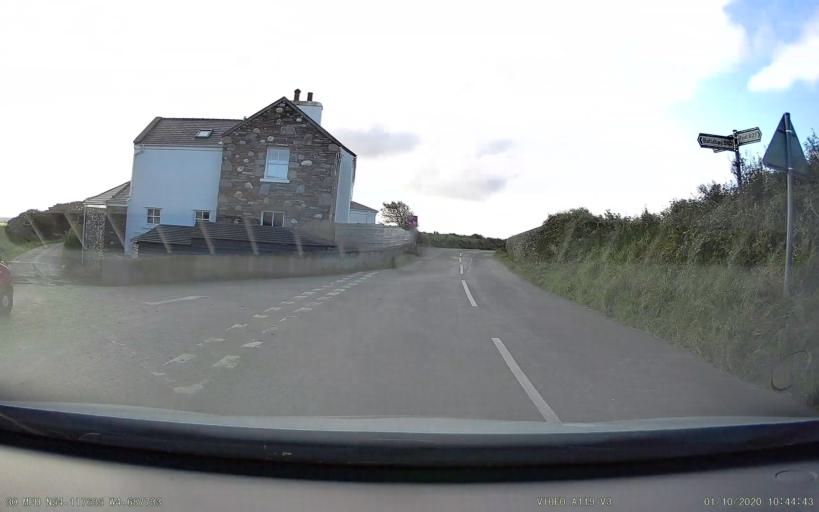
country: IM
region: Castletown
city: Castletown
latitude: 54.1176
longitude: -4.6877
